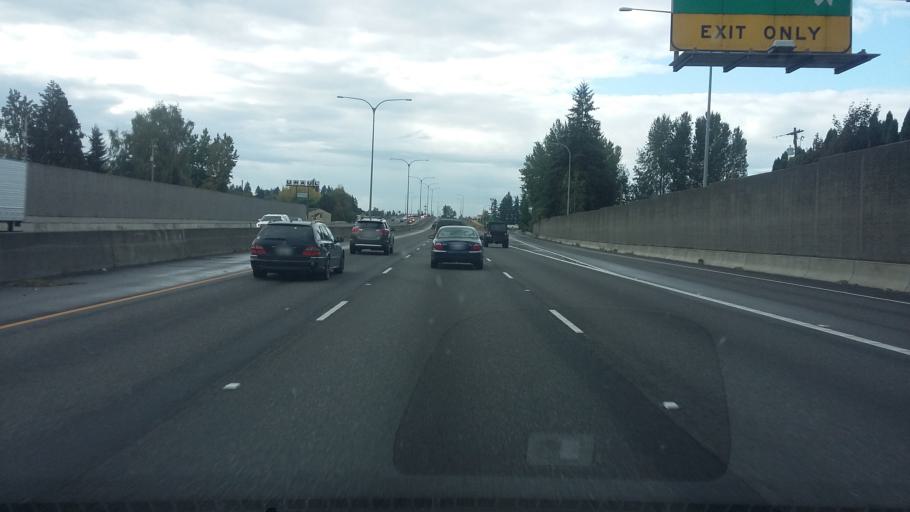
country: US
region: Washington
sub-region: Clark County
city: Hazel Dell
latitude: 45.6839
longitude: -122.6647
